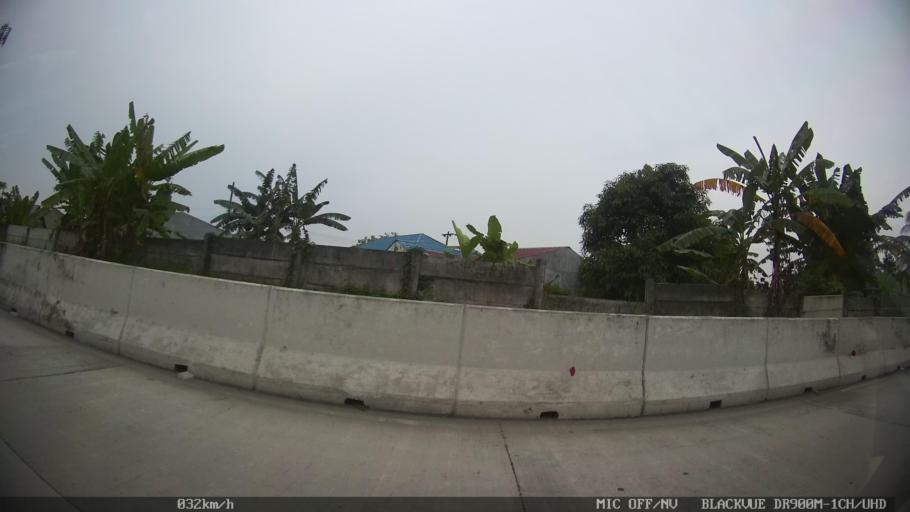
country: ID
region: North Sumatra
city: Deli Tua
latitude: 3.5405
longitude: 98.7238
